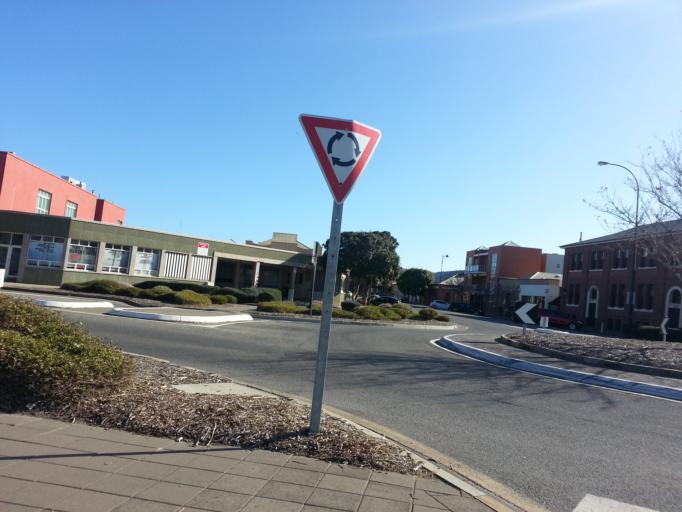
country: AU
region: South Australia
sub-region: Port Adelaide Enfield
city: Birkenhead
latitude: -34.8423
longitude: 138.5078
